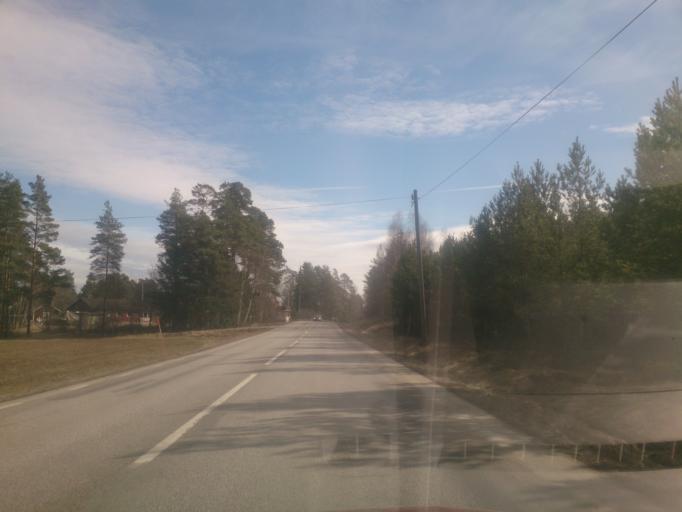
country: SE
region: OEstergoetland
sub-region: Finspangs Kommun
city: Finspang
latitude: 58.6581
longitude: 15.7985
